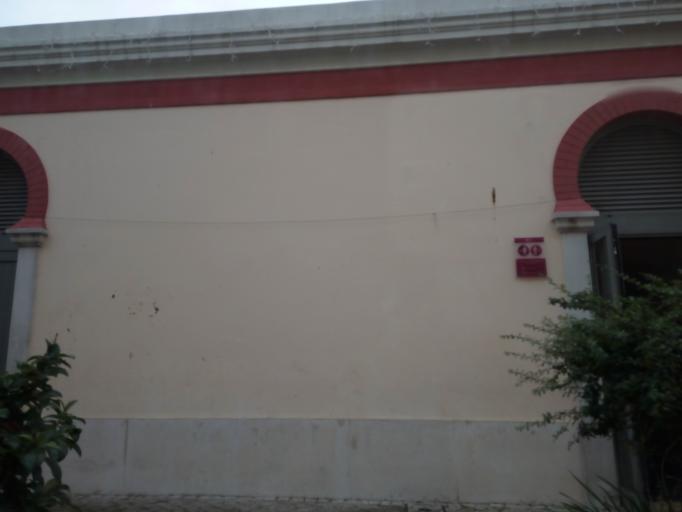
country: PT
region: Faro
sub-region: Loule
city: Loule
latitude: 37.1382
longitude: -8.0228
